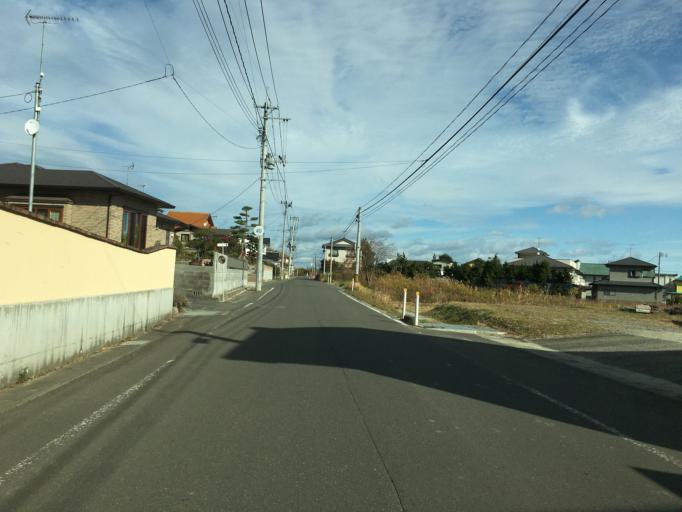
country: JP
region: Miyagi
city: Watari
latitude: 37.9247
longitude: 140.8955
